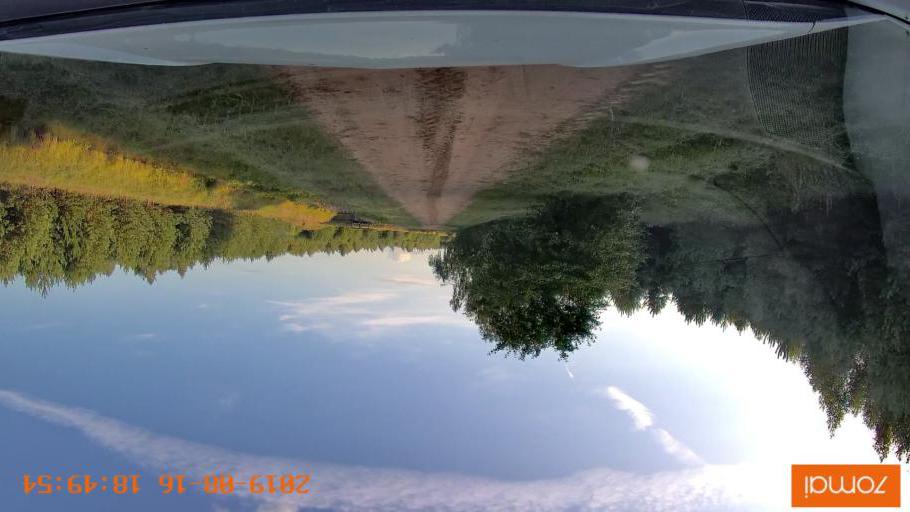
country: BY
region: Mogilev
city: Asipovichy
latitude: 53.2394
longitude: 28.6647
